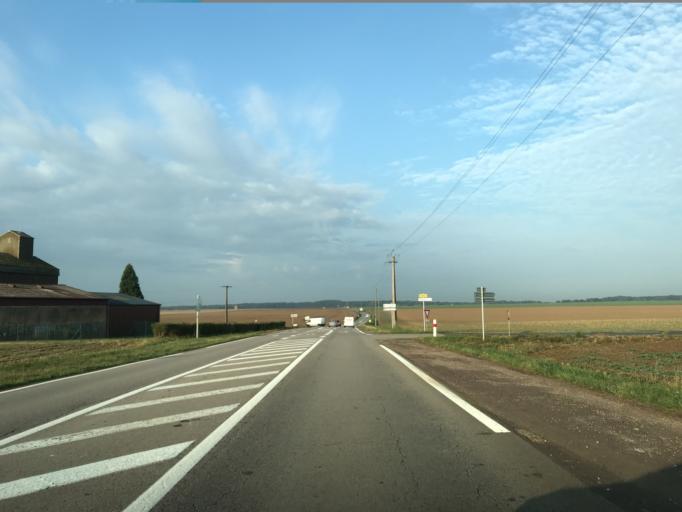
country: FR
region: Haute-Normandie
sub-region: Departement de l'Eure
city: Gravigny
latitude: 49.0725
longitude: 1.2238
